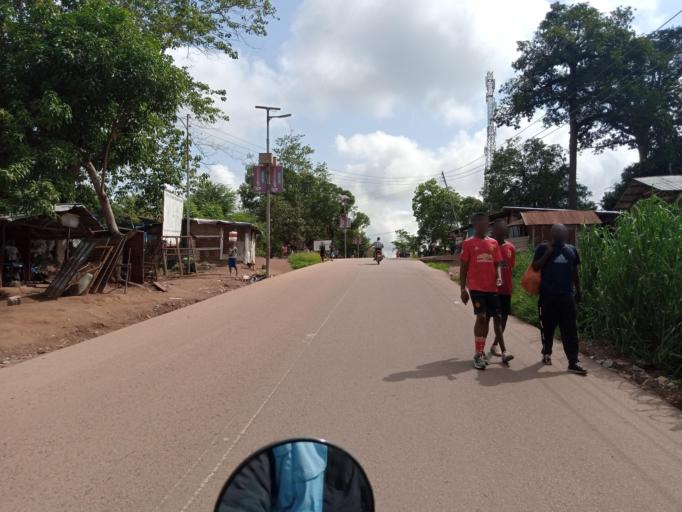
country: SL
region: Southern Province
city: Bo
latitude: 7.9801
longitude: -11.7385
